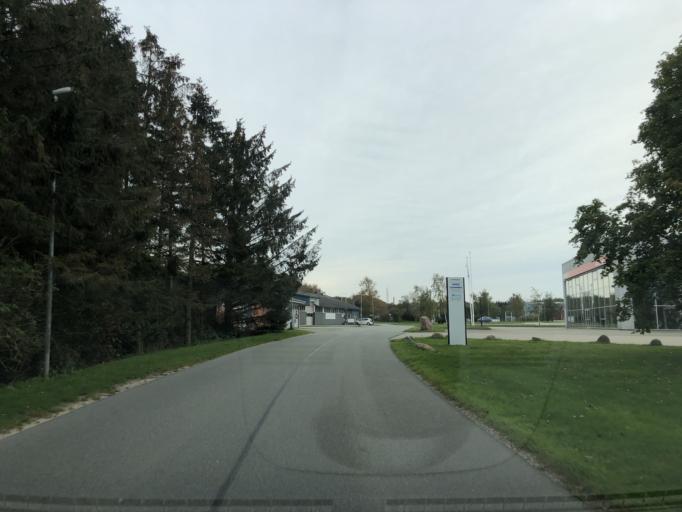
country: DK
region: Central Jutland
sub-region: Syddjurs Kommune
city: Hornslet
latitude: 56.3061
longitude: 10.3129
